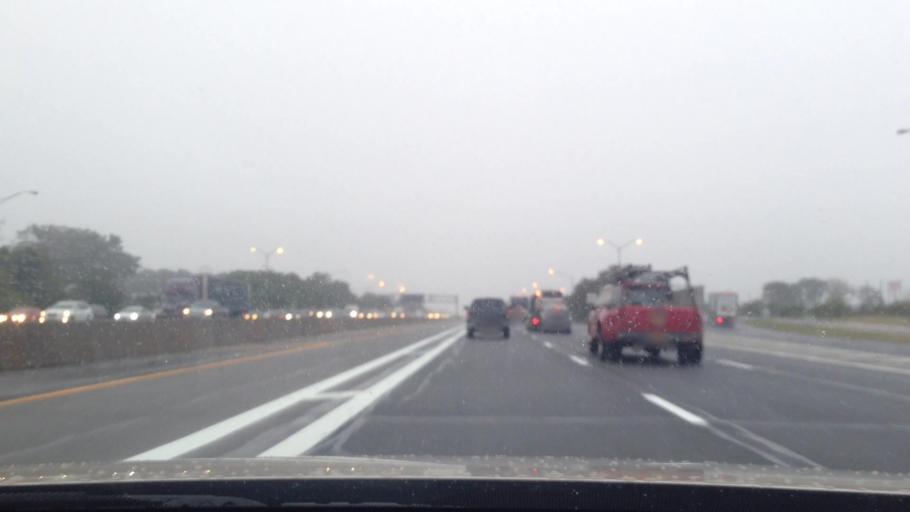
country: US
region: New York
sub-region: Suffolk County
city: Holbrook
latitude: 40.8196
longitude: -73.0644
